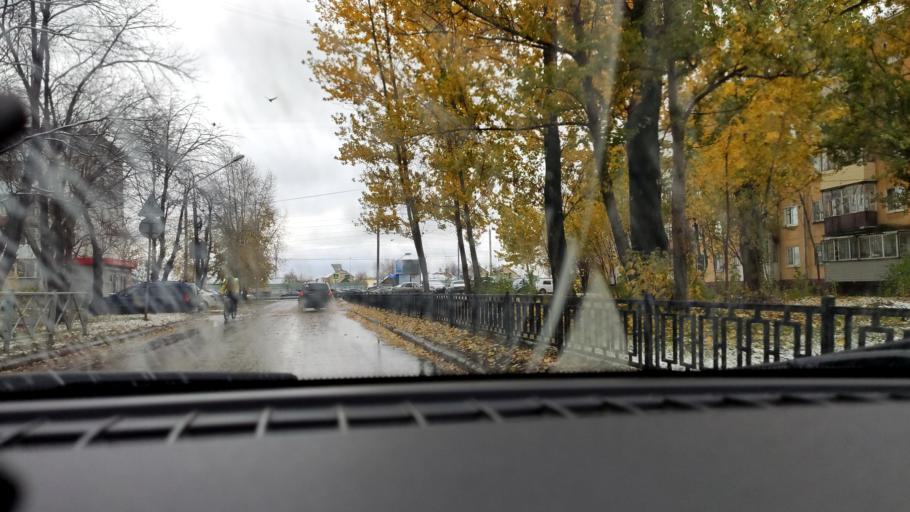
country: RU
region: Perm
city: Perm
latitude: 57.9941
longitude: 56.3006
